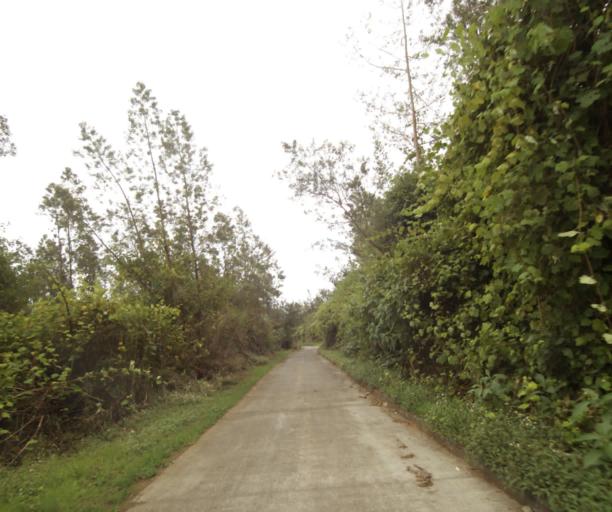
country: RE
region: Reunion
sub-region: Reunion
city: Saint-Paul
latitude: -21.0159
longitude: 55.3531
